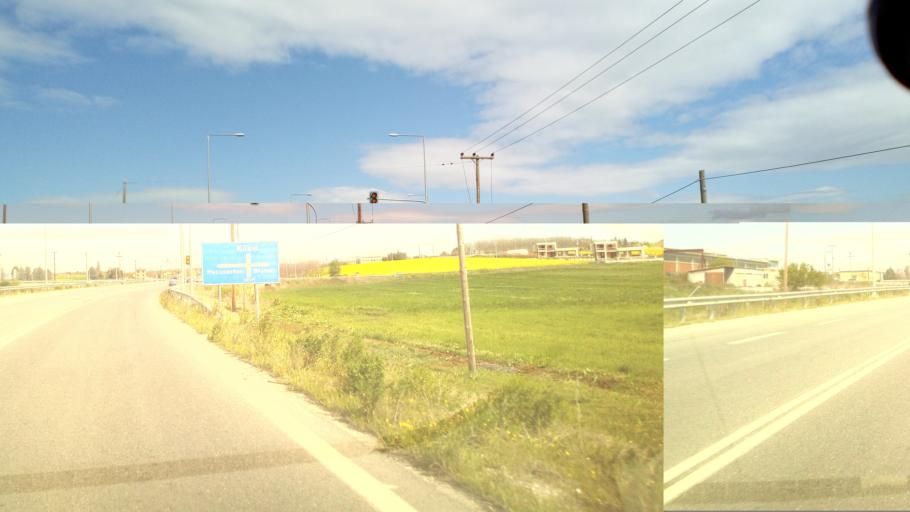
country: GR
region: Central Macedonia
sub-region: Nomos Thessalonikis
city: Drymos
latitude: 40.7742
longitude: 22.9471
